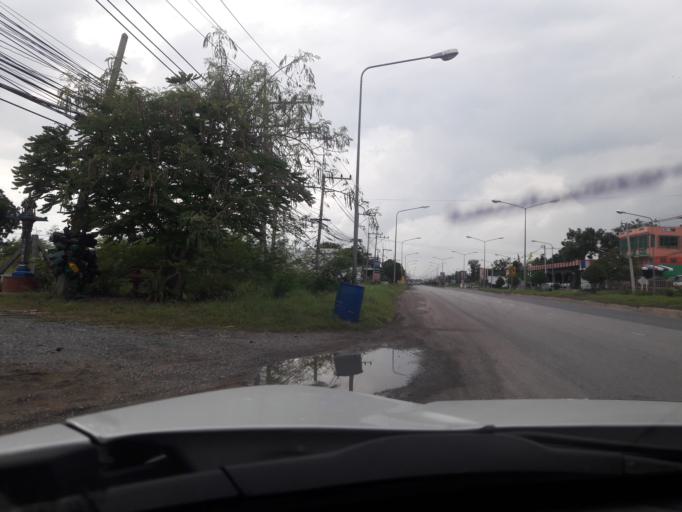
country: TH
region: Lop Buri
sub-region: Amphoe Tha Luang
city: Tha Luang
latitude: 15.0669
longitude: 101.1187
